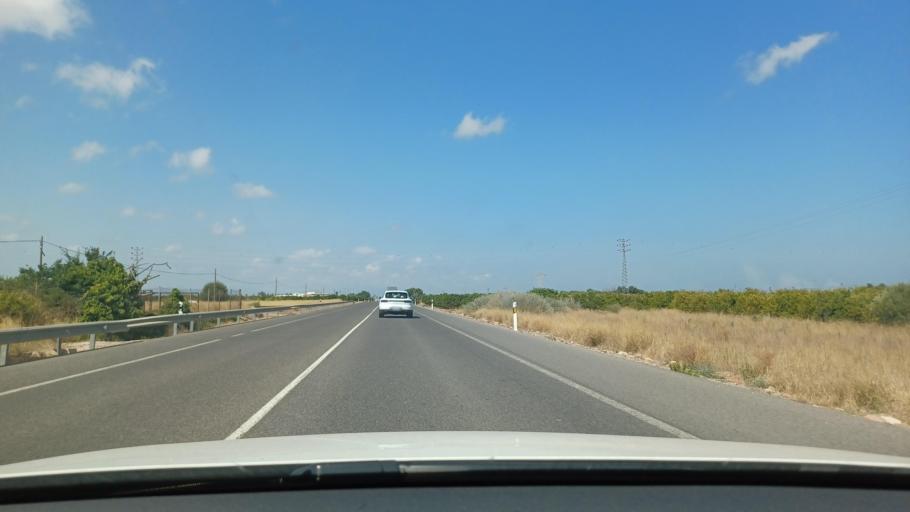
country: ES
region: Valencia
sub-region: Provincia de Castello
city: Moncofar
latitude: 39.8052
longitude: -0.1734
